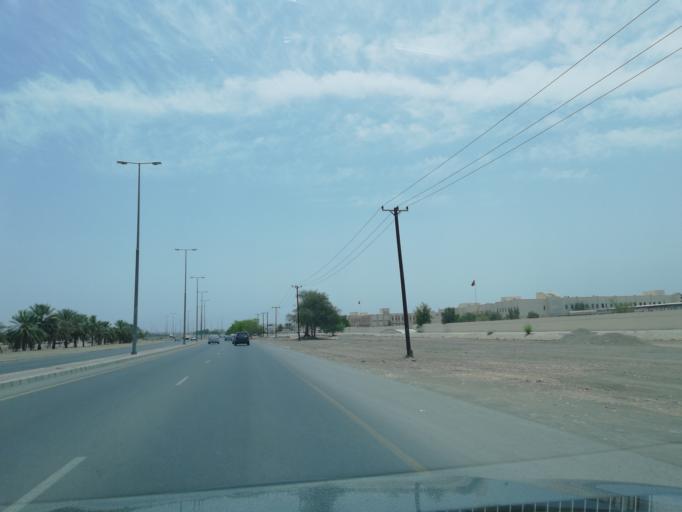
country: OM
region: Muhafazat Masqat
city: As Sib al Jadidah
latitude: 23.6730
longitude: 58.1642
